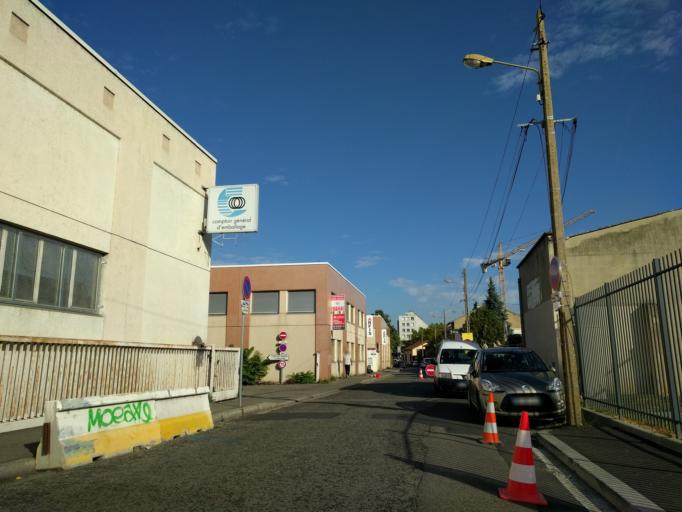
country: FR
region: Rhone-Alpes
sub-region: Departement du Rhone
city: Villeurbanne
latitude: 45.7581
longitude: 4.9018
